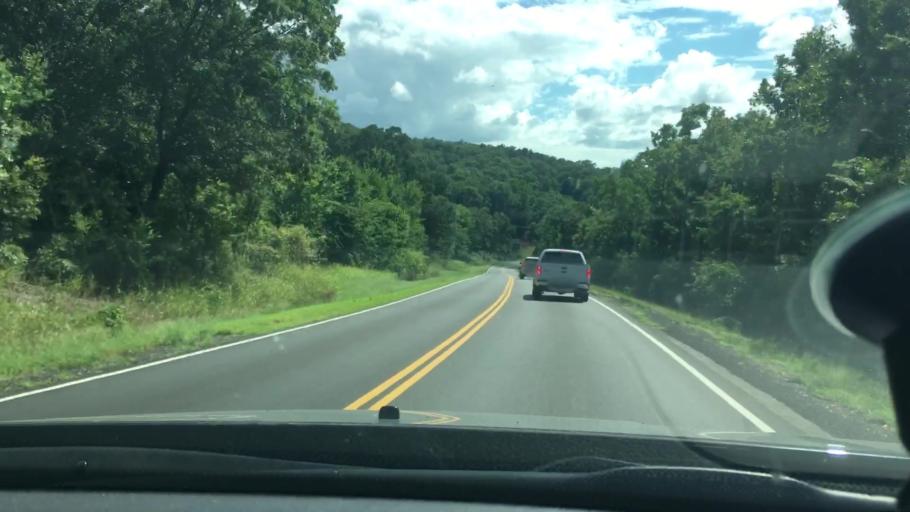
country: US
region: Oklahoma
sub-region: Sequoyah County
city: Vian
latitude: 35.6522
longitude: -94.9534
